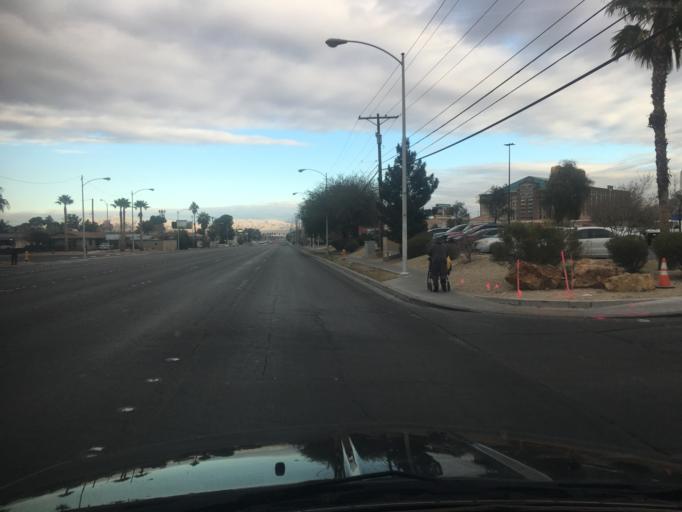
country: US
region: Nevada
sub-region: Clark County
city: Whitney
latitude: 36.1091
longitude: -115.0643
